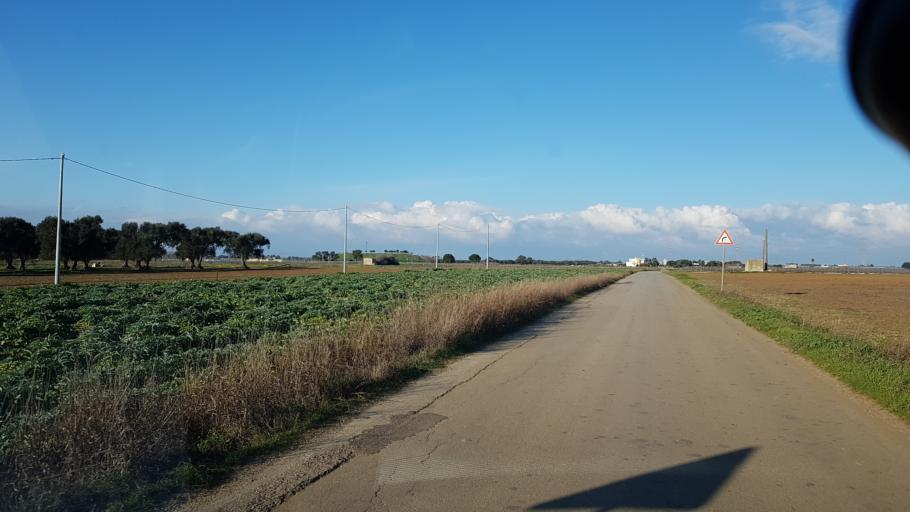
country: IT
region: Apulia
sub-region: Provincia di Brindisi
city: Tuturano
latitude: 40.5723
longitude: 17.8995
